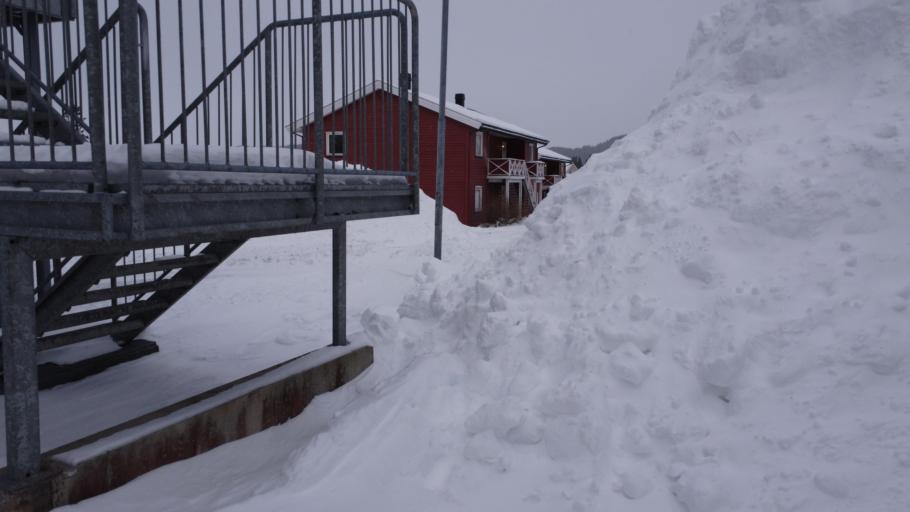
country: NO
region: Nordland
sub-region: Rana
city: Mo i Rana
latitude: 66.3298
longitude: 14.1540
